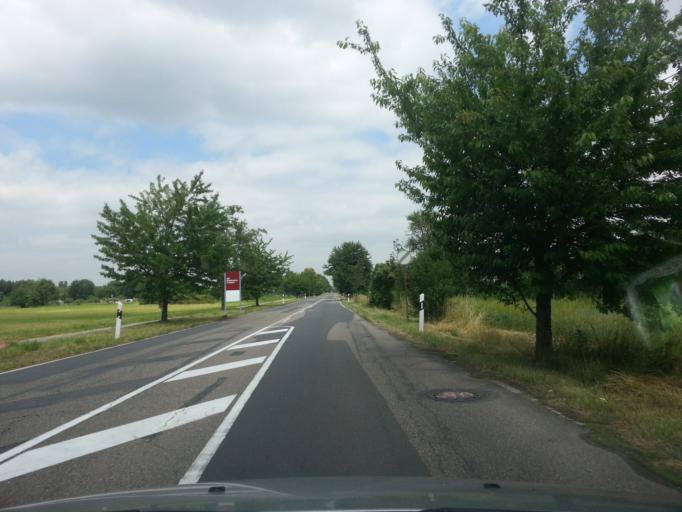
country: DE
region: Baden-Wuerttemberg
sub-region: Karlsruhe Region
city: Ketsch
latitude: 49.3796
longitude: 8.5269
